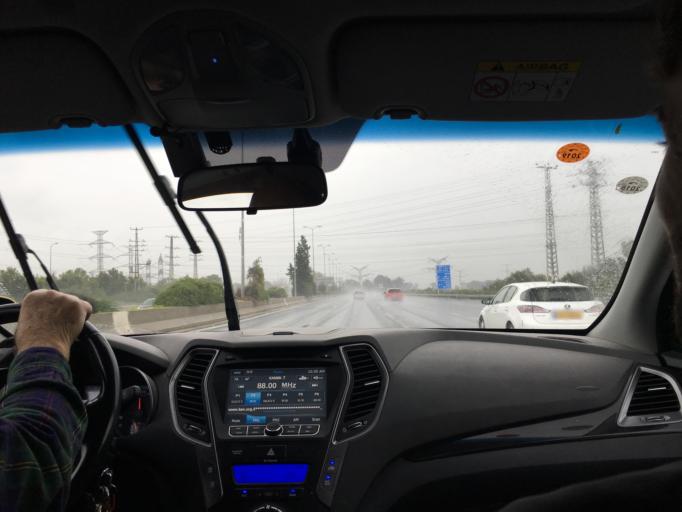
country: IL
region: Central District
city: Petah Tiqwa
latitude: 32.1192
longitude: 34.8836
